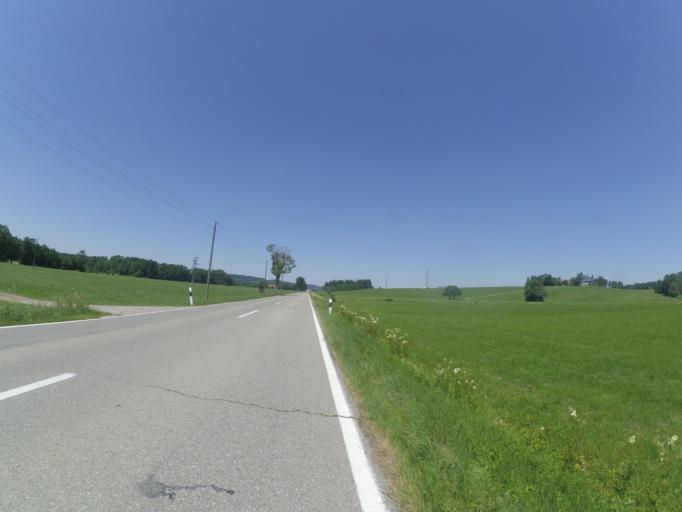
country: DE
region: Bavaria
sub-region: Swabia
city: Bohen
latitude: 47.8998
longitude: 10.3184
